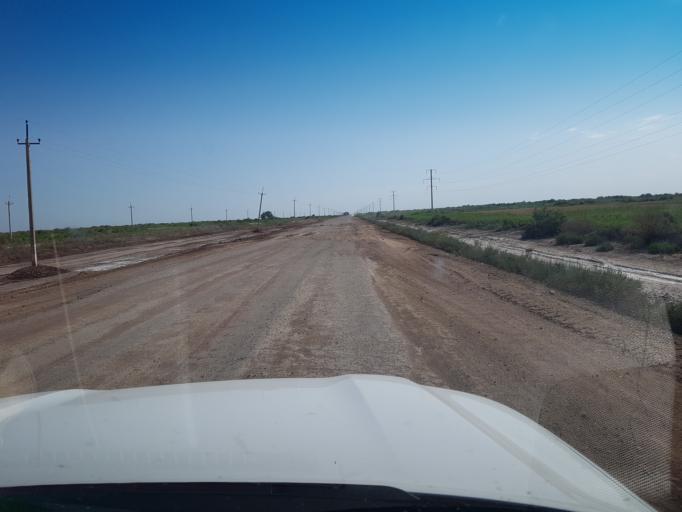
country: TM
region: Dasoguz
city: Koeneuergench
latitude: 42.1179
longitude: 58.9277
